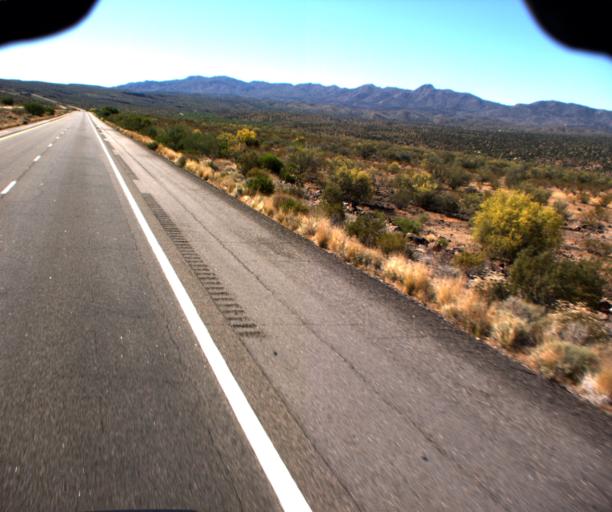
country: US
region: Arizona
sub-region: Yavapai County
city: Bagdad
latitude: 34.5221
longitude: -113.4245
